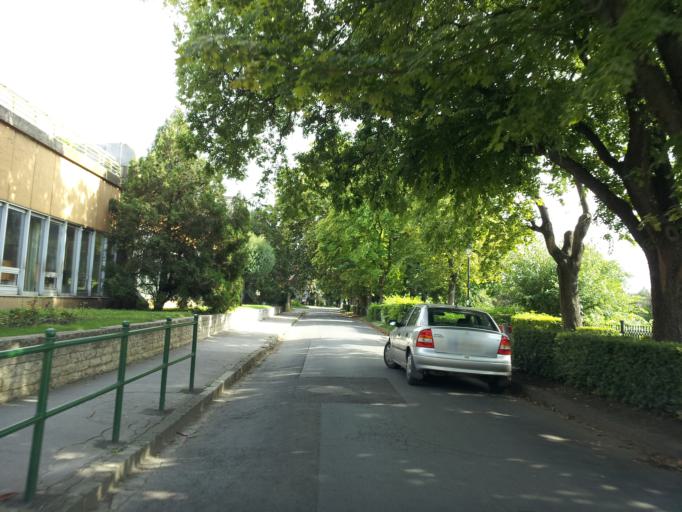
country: HU
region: Pest
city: Vac
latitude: 47.7757
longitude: 19.1273
